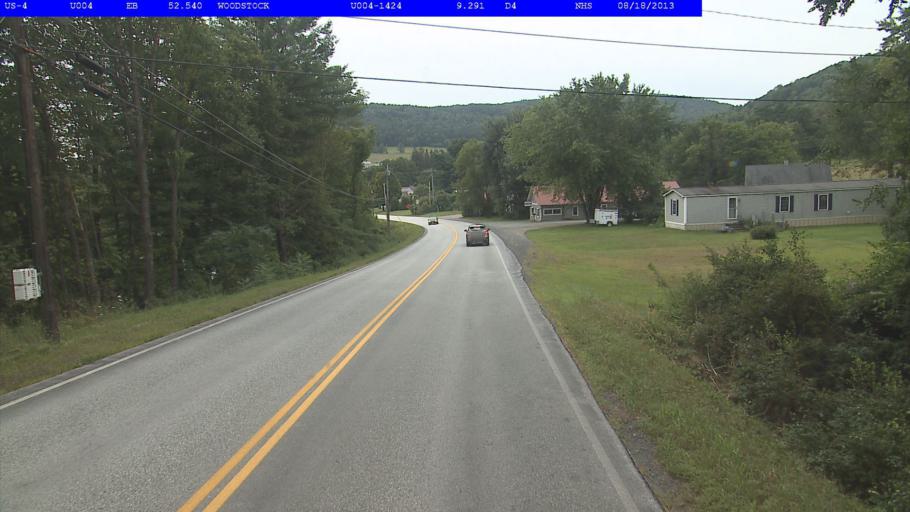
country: US
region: Vermont
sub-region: Windsor County
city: Woodstock
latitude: 43.6346
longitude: -72.4708
